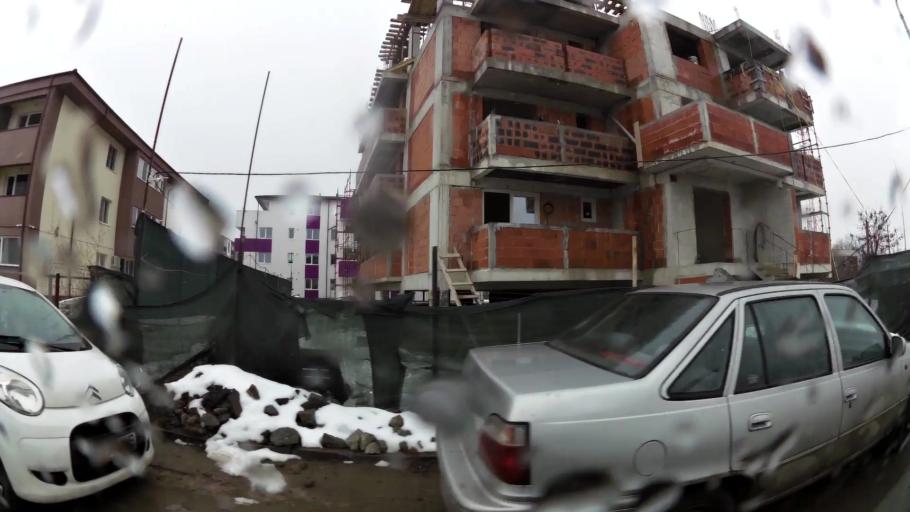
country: RO
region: Ilfov
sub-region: Comuna Glina
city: Catelu
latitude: 44.4184
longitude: 26.1912
